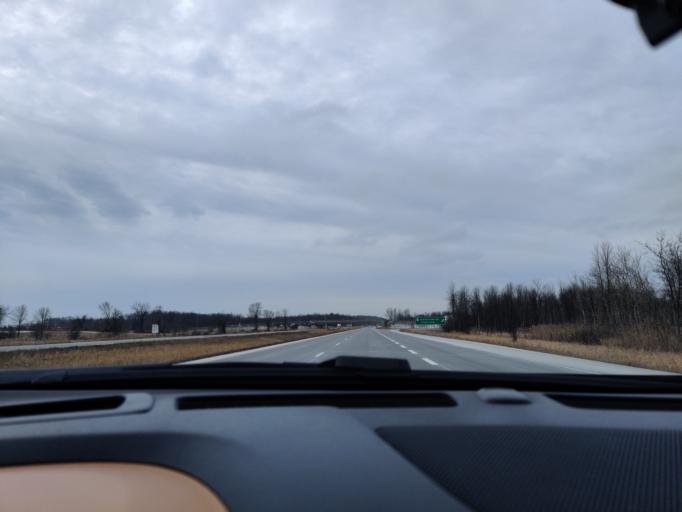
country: CA
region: Ontario
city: Cornwall
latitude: 45.0933
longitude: -74.5875
